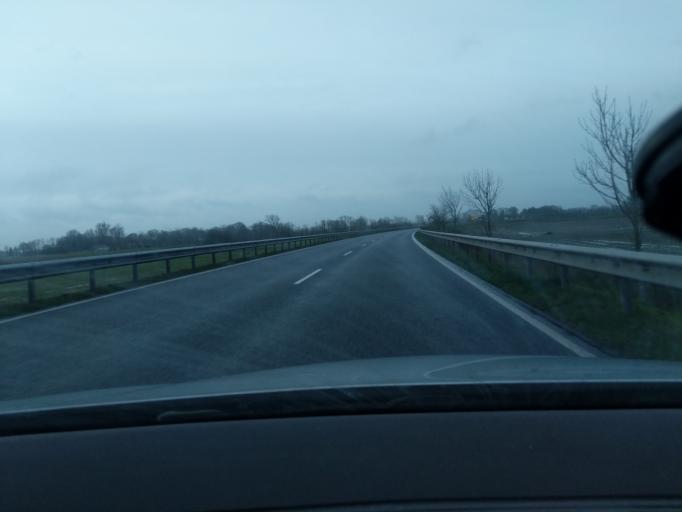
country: DE
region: Lower Saxony
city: Otterndorf
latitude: 53.7981
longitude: 8.9136
